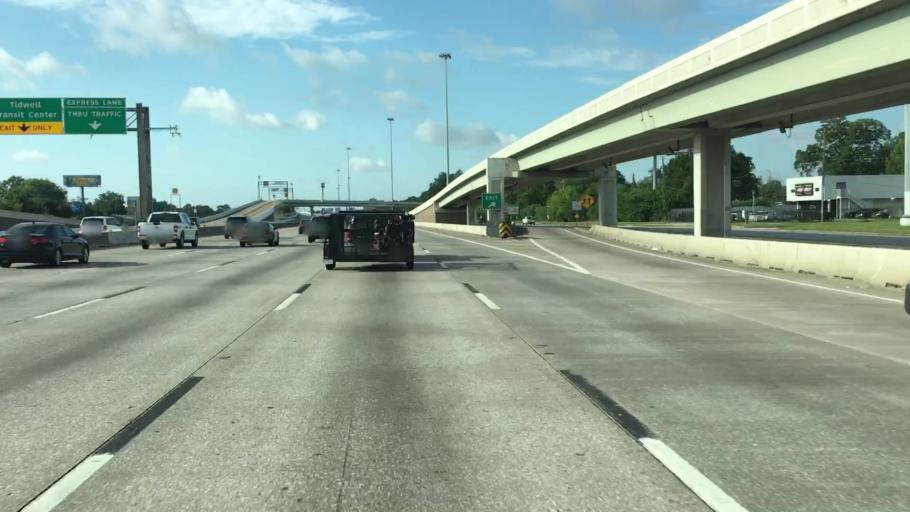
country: US
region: Texas
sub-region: Harris County
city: Aldine
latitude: 29.8548
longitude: -95.3340
